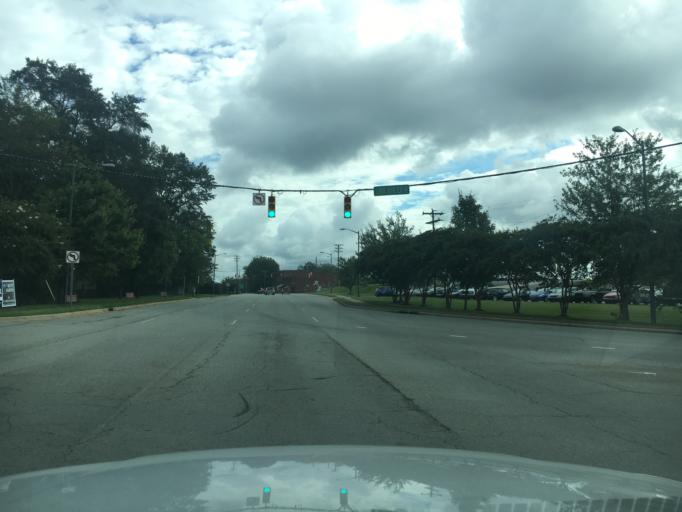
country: US
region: North Carolina
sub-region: Catawba County
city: Hickory
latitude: 35.7380
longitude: -81.3242
